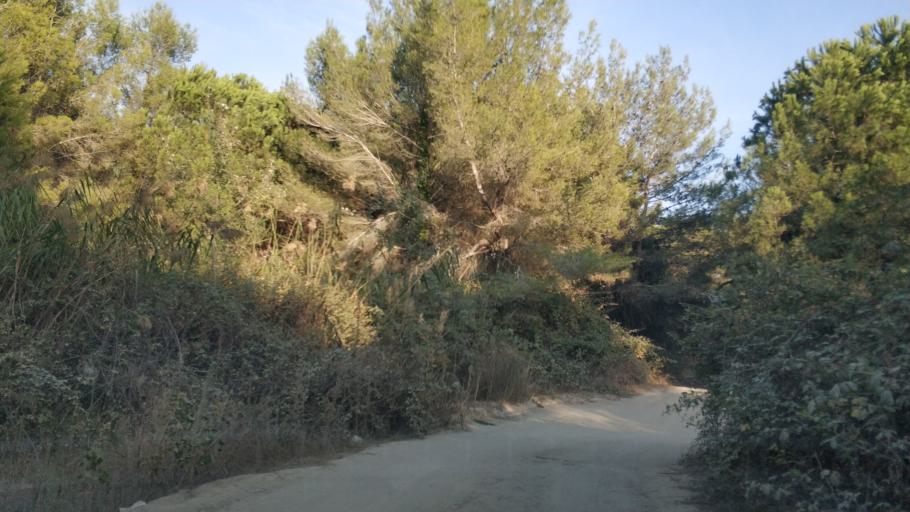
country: AL
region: Fier
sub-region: Rrethi i Lushnjes
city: Divjake
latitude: 40.9531
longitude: 19.4744
